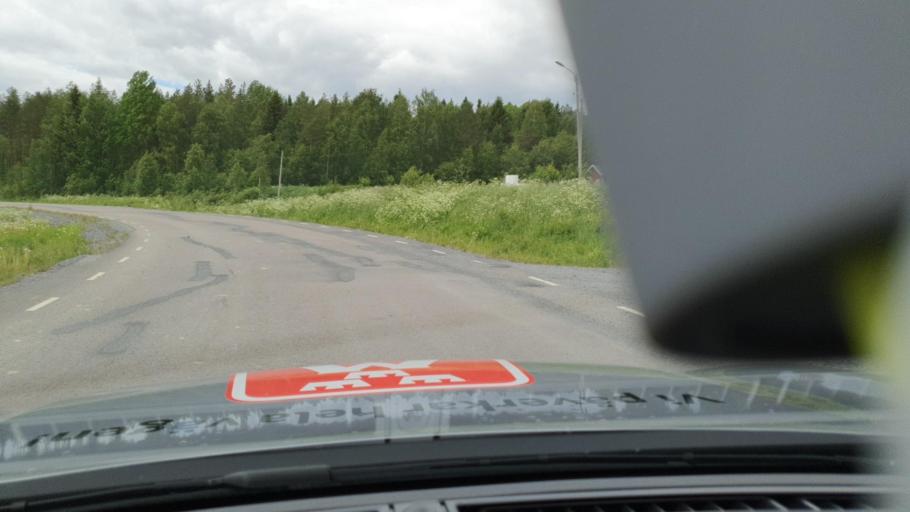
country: SE
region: Norrbotten
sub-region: Lulea Kommun
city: Sodra Sunderbyn
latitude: 65.8382
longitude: 21.9484
